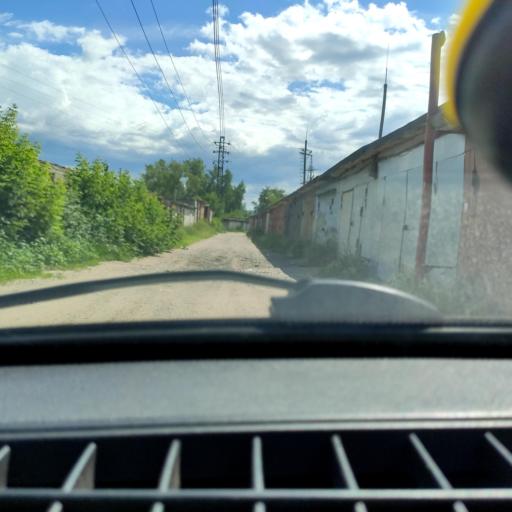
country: RU
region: Samara
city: Zhigulevsk
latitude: 53.4697
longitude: 49.5180
